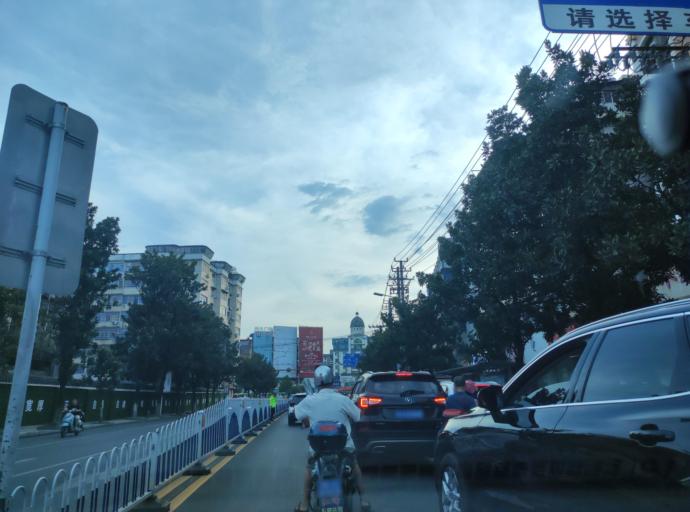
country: CN
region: Jiangxi Sheng
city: Pingxiang
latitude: 27.6310
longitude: 113.8521
